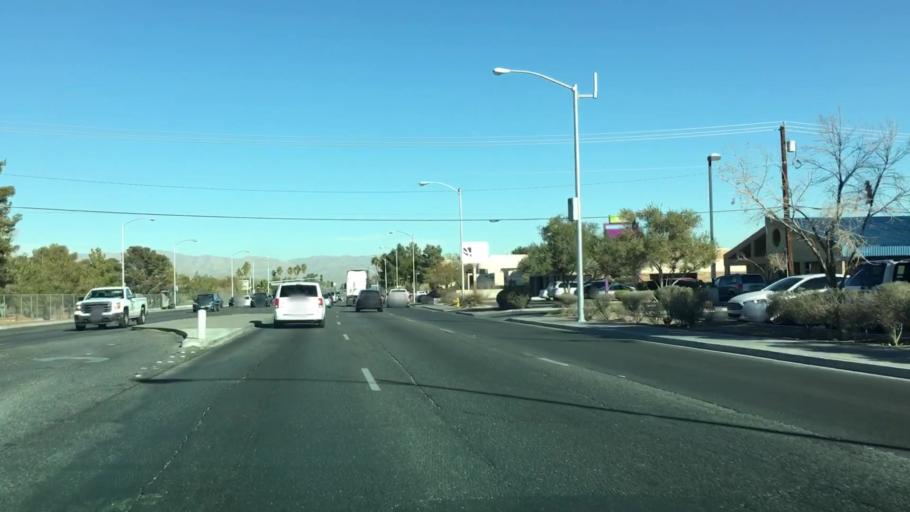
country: US
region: Nevada
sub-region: Clark County
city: Winchester
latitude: 36.1161
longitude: -115.1191
